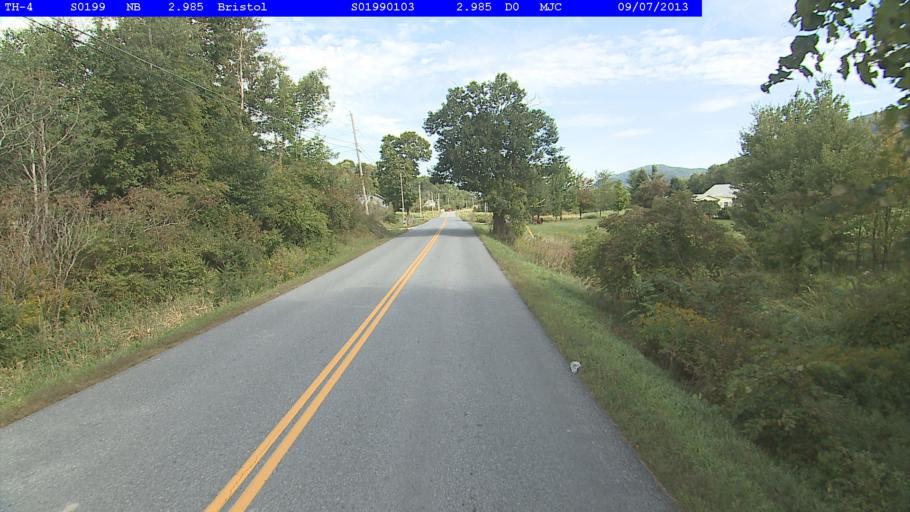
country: US
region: Vermont
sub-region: Addison County
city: Bristol
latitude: 44.1712
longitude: -73.1016
